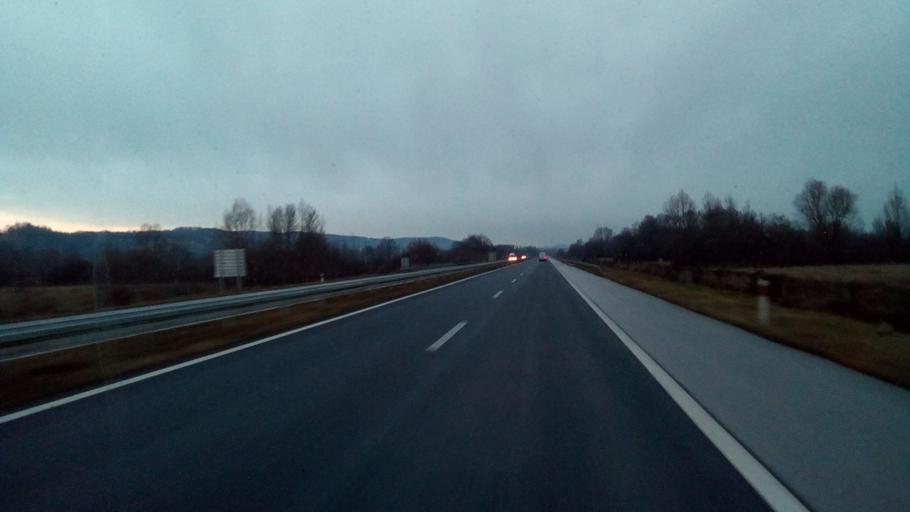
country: HR
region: Zagrebacka
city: Brckovljani
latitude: 45.9272
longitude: 16.2718
